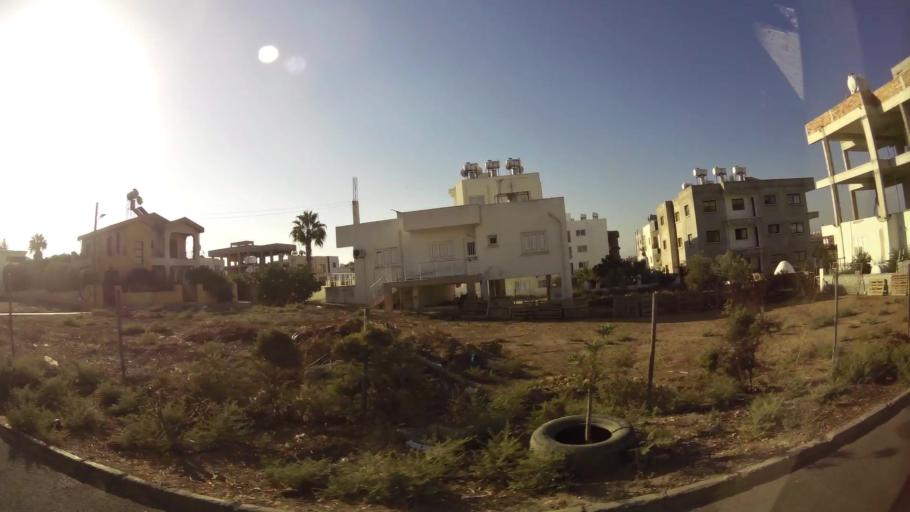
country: CY
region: Lefkosia
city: Nicosia
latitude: 35.2138
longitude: 33.2955
